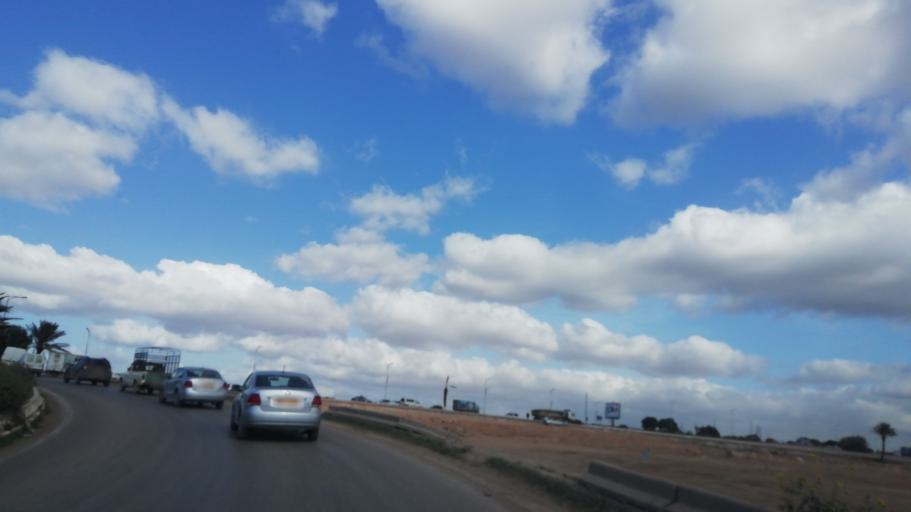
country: DZ
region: Oran
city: Es Senia
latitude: 35.6234
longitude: -0.5875
